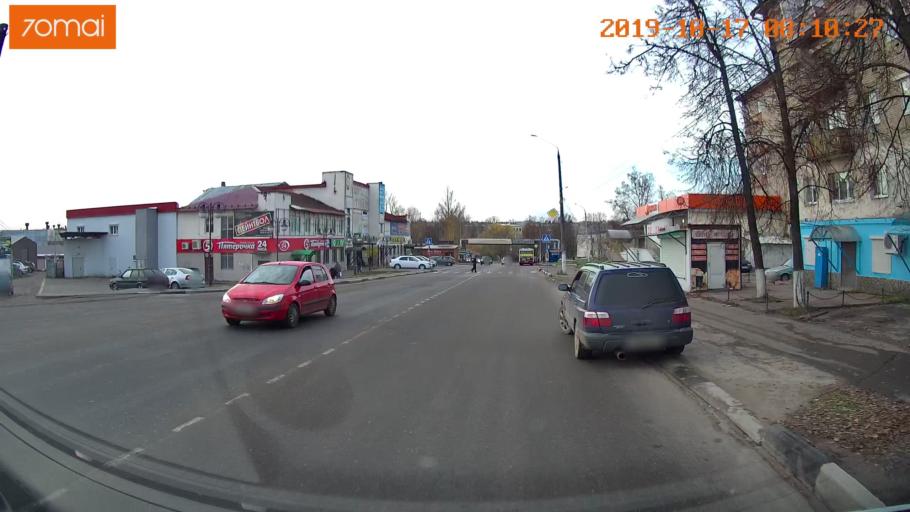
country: RU
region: Vladimir
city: Kol'chugino
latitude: 56.3078
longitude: 39.3776
